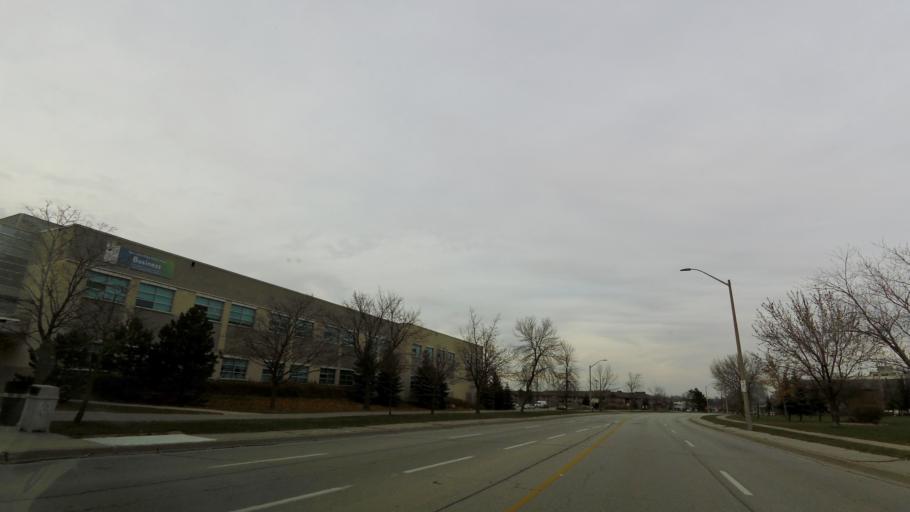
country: CA
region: Ontario
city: Mississauga
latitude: 43.6121
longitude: -79.6200
